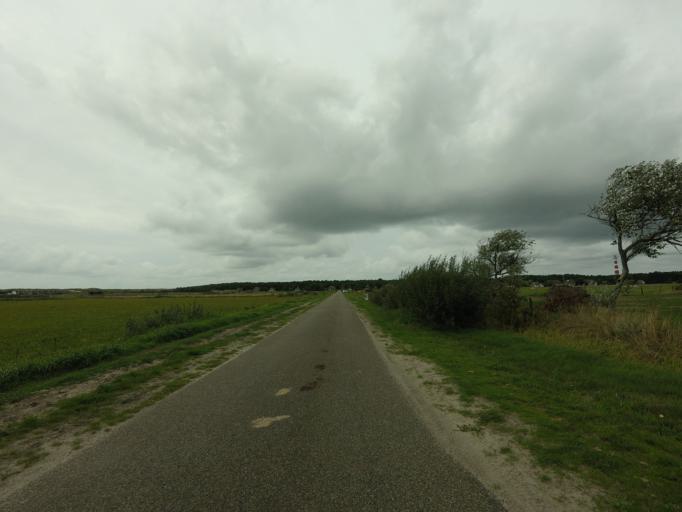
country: NL
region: Friesland
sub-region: Gemeente Ameland
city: Hollum
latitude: 53.4430
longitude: 5.6321
